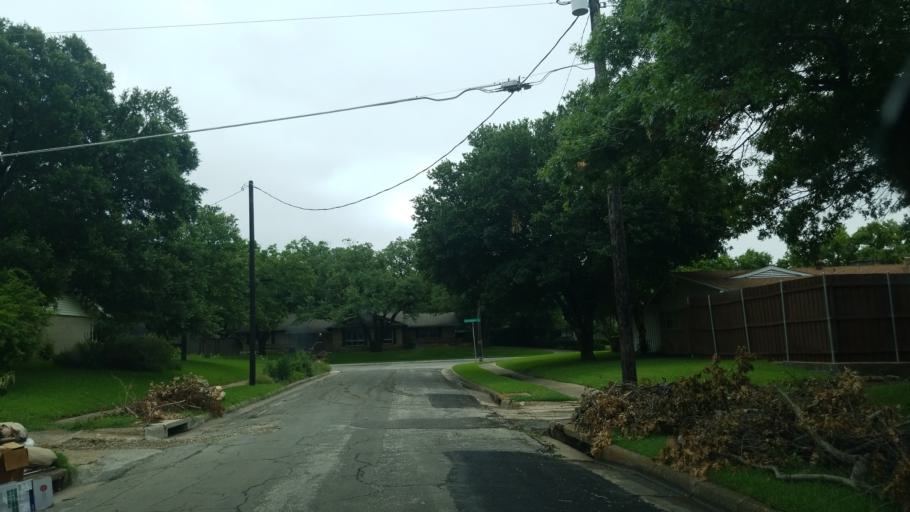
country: US
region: Texas
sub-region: Dallas County
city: Farmers Branch
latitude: 32.9056
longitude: -96.8662
